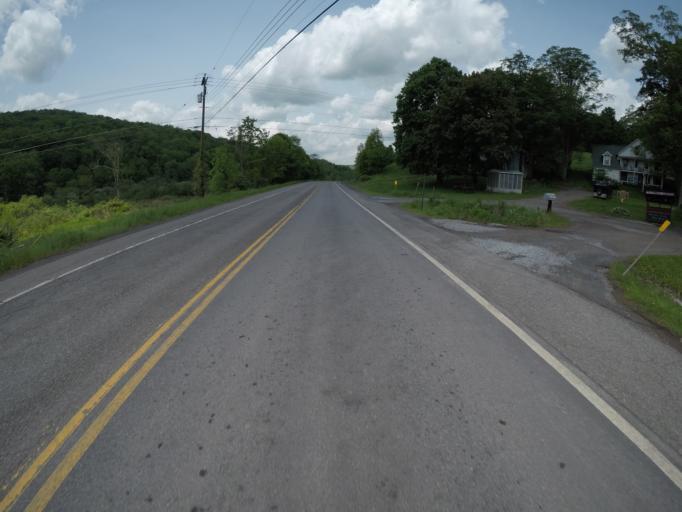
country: US
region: New York
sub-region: Delaware County
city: Stamford
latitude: 42.1906
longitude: -74.5986
